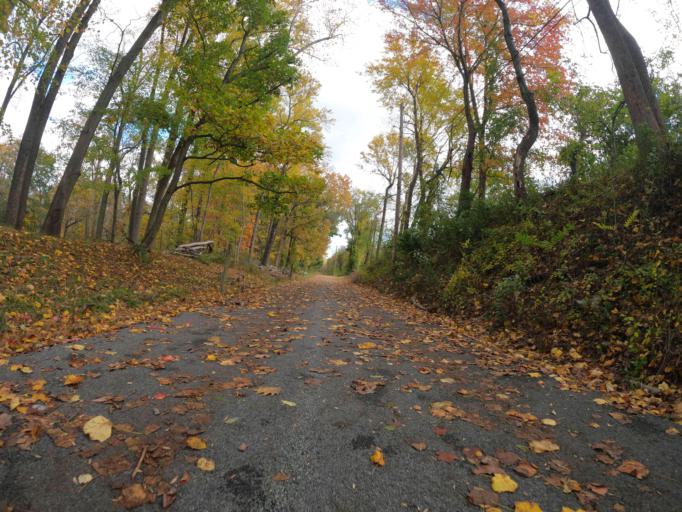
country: US
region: Maryland
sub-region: Carroll County
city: Mount Airy
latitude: 39.3706
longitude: -77.1350
